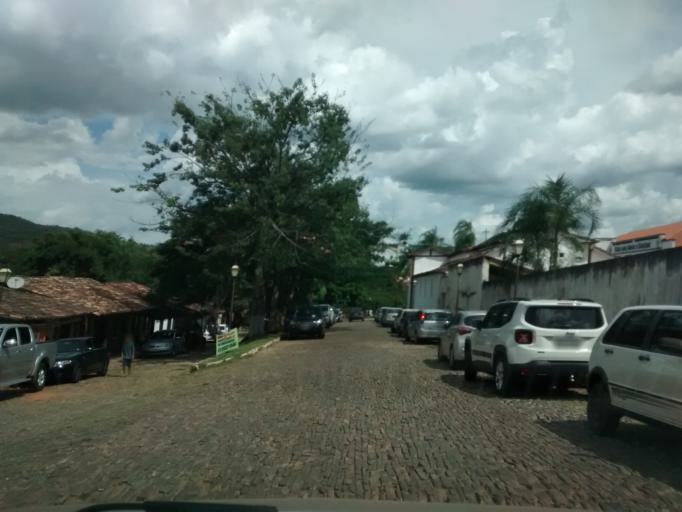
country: BR
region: Goias
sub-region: Pirenopolis
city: Pirenopolis
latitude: -15.8486
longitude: -48.9594
